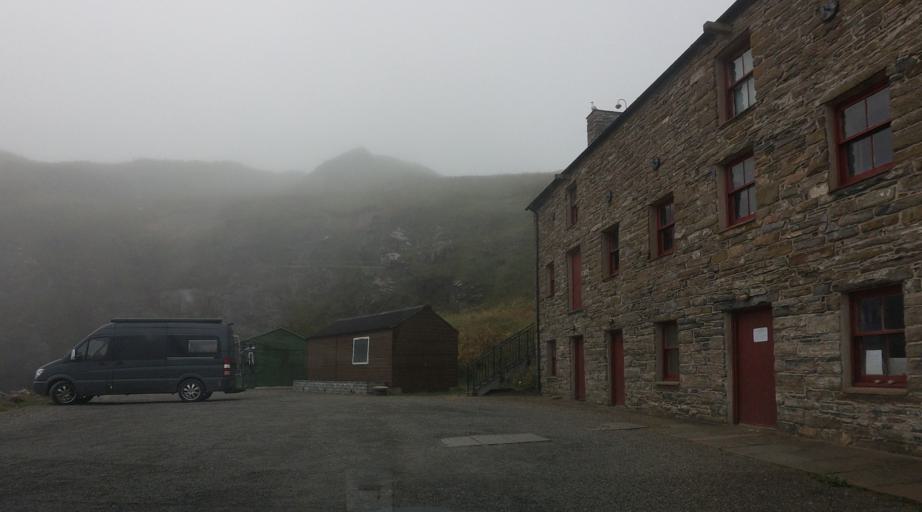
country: GB
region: Scotland
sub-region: Highland
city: Wick
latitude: 58.2959
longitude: -3.2913
